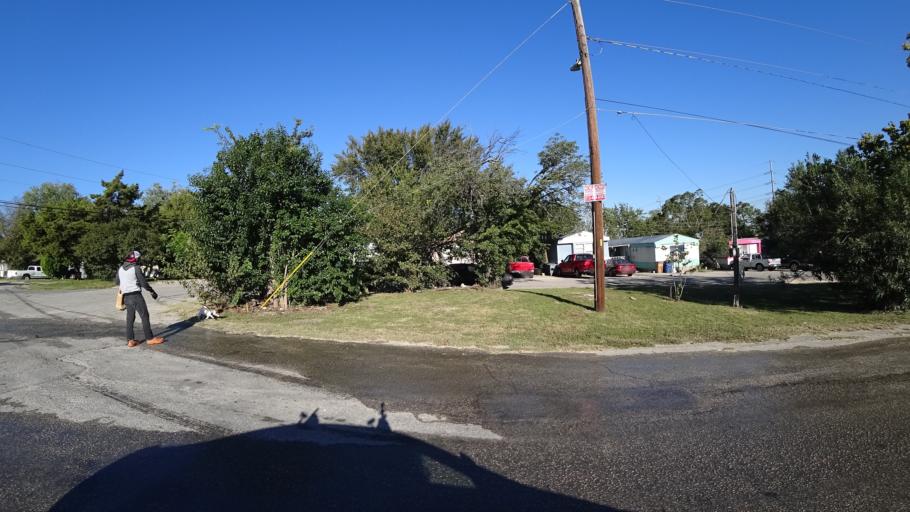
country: US
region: Texas
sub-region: Travis County
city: Austin
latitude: 30.2192
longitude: -97.6935
